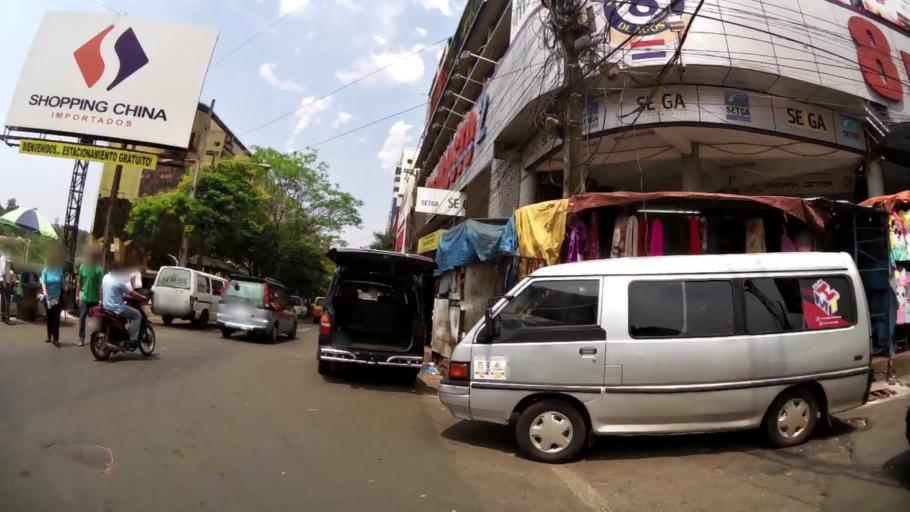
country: PY
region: Alto Parana
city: Ciudad del Este
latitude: -25.5115
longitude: -54.6071
